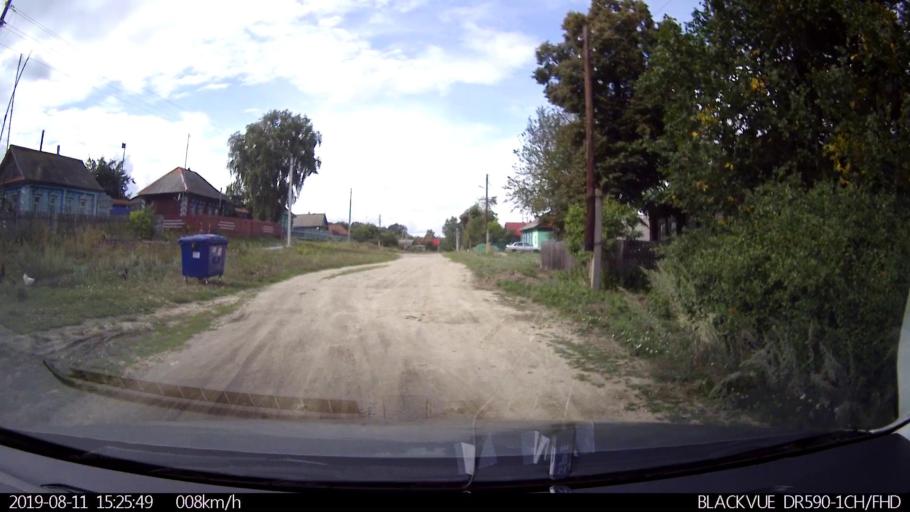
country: RU
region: Ulyanovsk
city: Ignatovka
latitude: 53.8495
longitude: 47.5767
